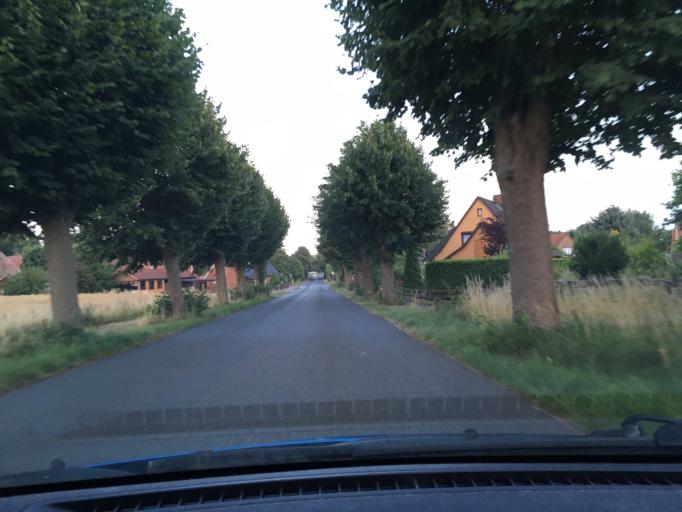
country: DE
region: Lower Saxony
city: Altenmedingen
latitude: 53.1326
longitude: 10.5965
